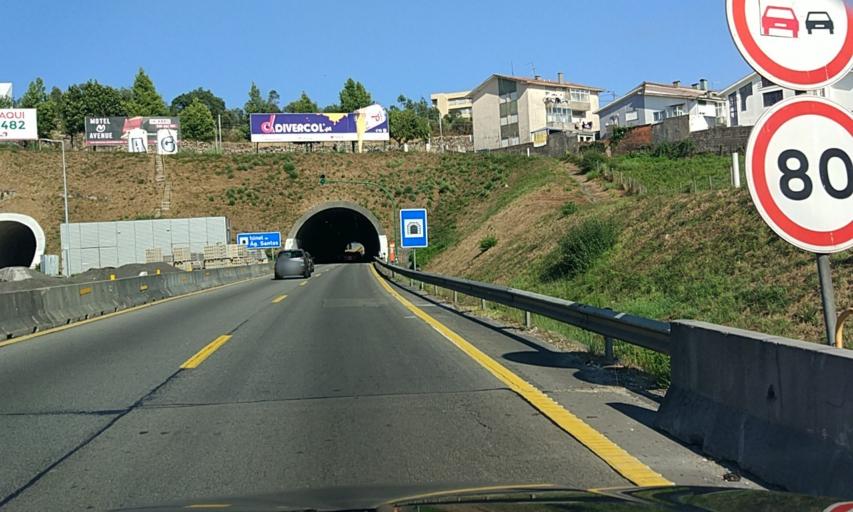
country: PT
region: Porto
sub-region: Maia
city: Pedroucos
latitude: 41.1980
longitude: -8.5789
